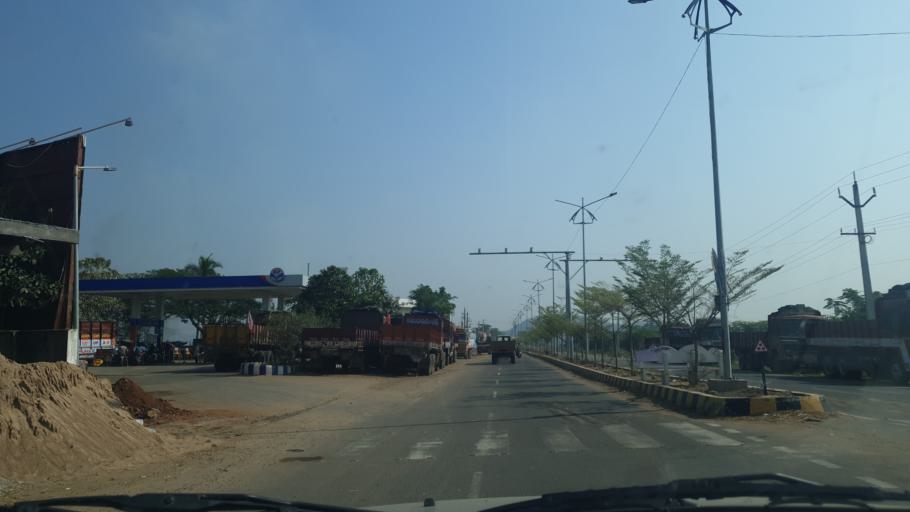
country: IN
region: Andhra Pradesh
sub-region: Srikakulam
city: Tekkali
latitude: 18.6142
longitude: 84.2369
